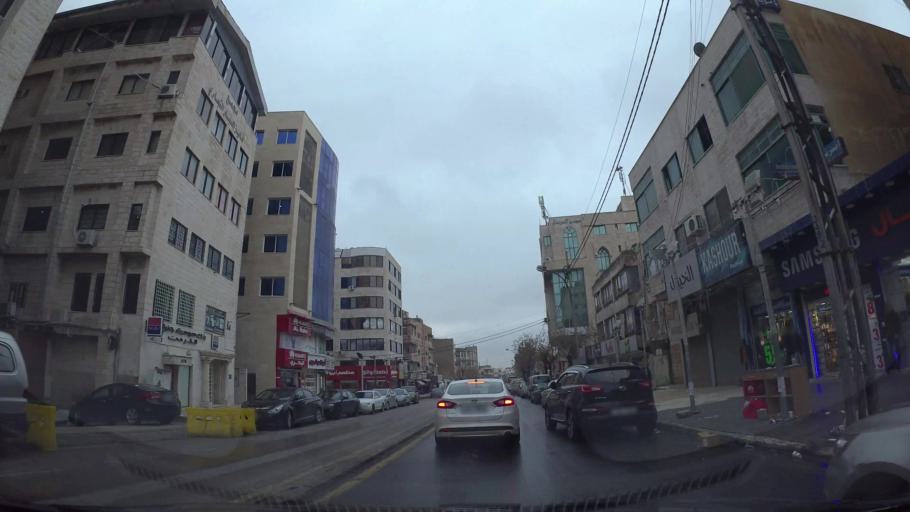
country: JO
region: Amman
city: Amman
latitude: 31.9653
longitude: 35.9210
